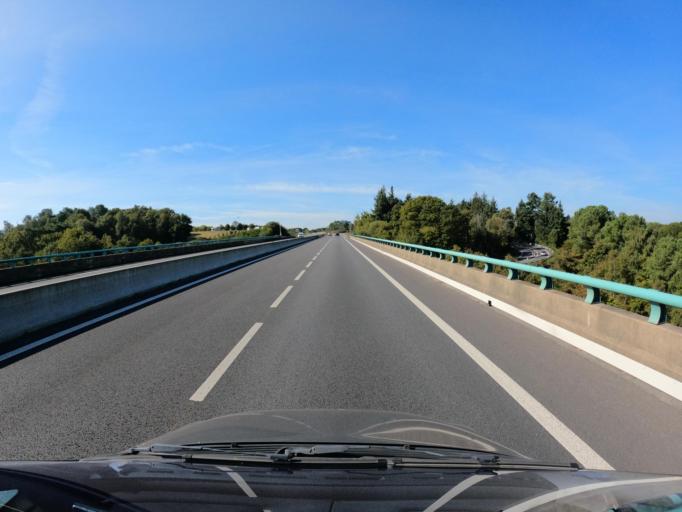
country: FR
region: Brittany
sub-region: Departement du Morbihan
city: Nivillac
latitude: 47.5317
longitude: -2.3022
